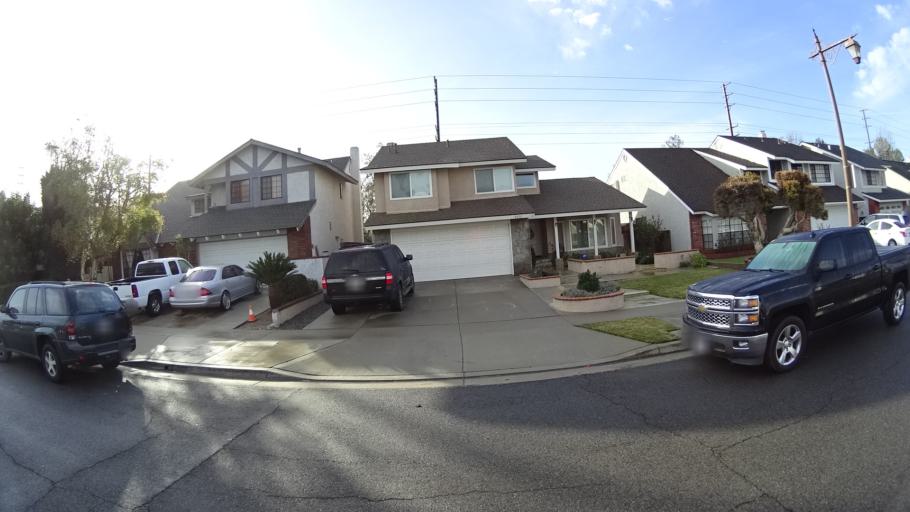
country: US
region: California
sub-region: Orange County
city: Yorba Linda
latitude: 33.8735
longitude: -117.7592
